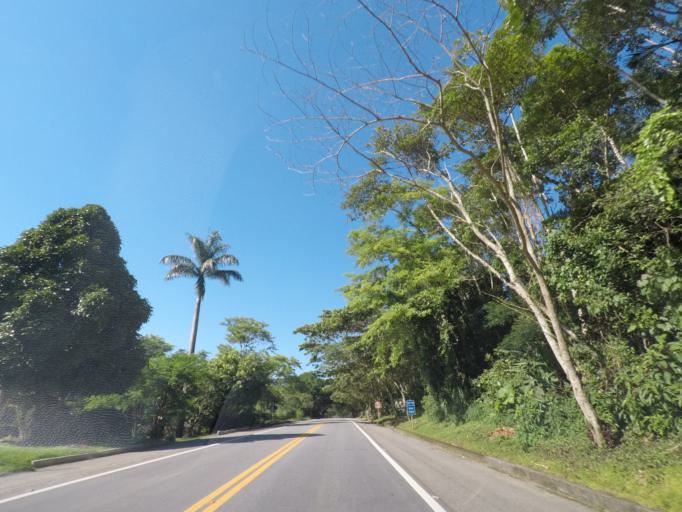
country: BR
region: Rio de Janeiro
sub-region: Parati
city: Paraty
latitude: -23.2921
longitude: -44.6977
